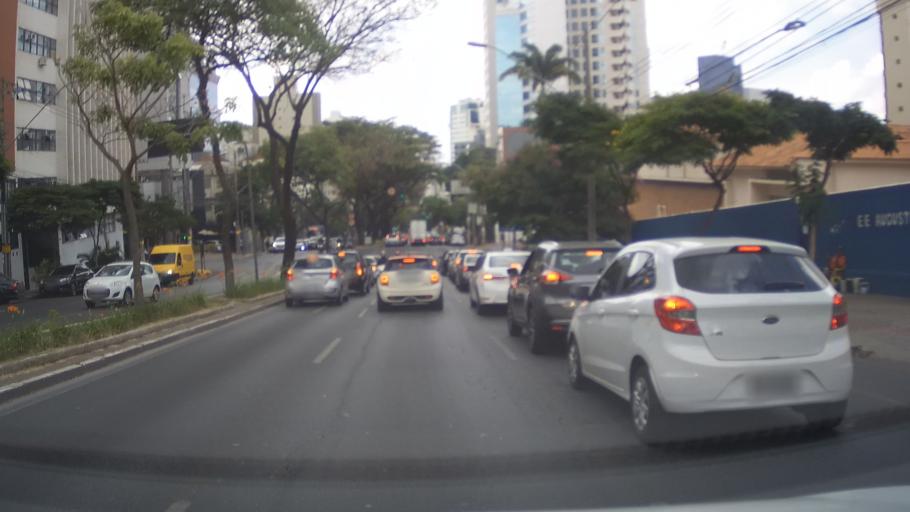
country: BR
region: Minas Gerais
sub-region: Belo Horizonte
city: Belo Horizonte
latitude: -19.9374
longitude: -43.9256
